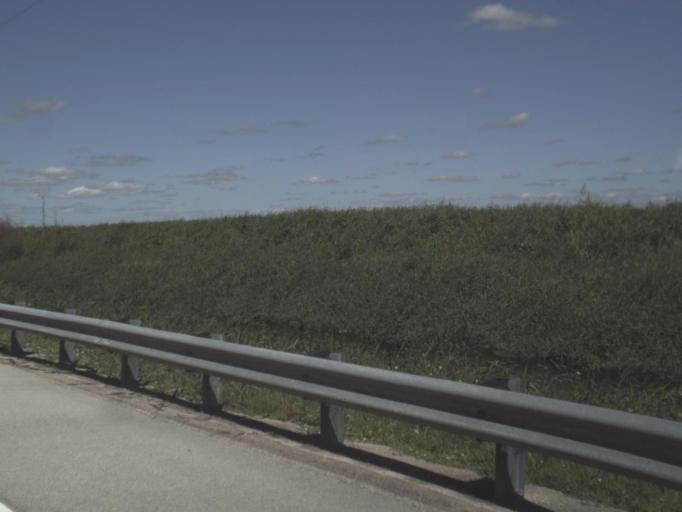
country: US
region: Florida
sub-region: Collier County
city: Lely Resort
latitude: 26.0113
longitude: -81.6178
